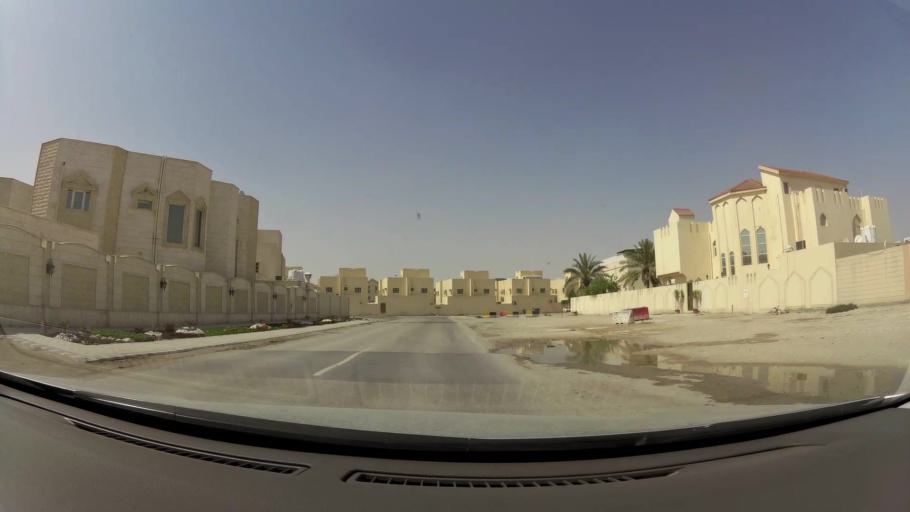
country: QA
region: Baladiyat Umm Salal
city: Umm Salal Muhammad
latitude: 25.3664
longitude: 51.4430
